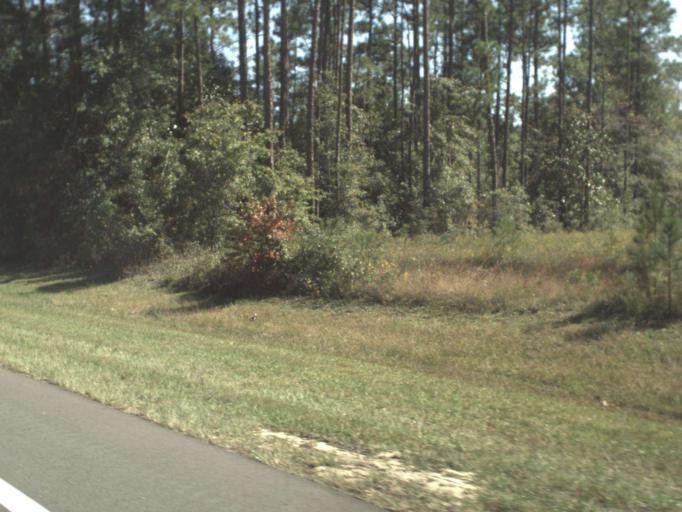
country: US
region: Florida
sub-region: Walton County
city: Freeport
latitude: 30.5049
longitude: -86.1552
